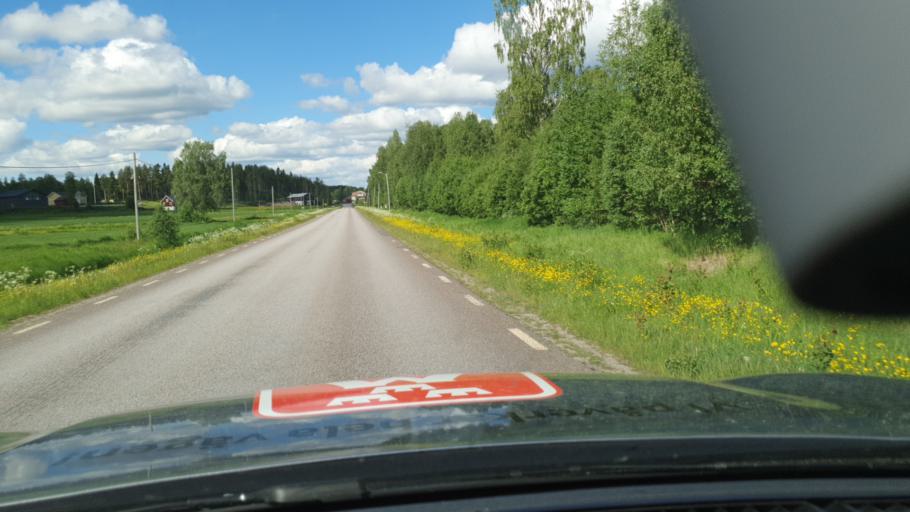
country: SE
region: Norrbotten
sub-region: Pitea Kommun
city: Norrfjarden
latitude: 65.5148
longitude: 21.5119
